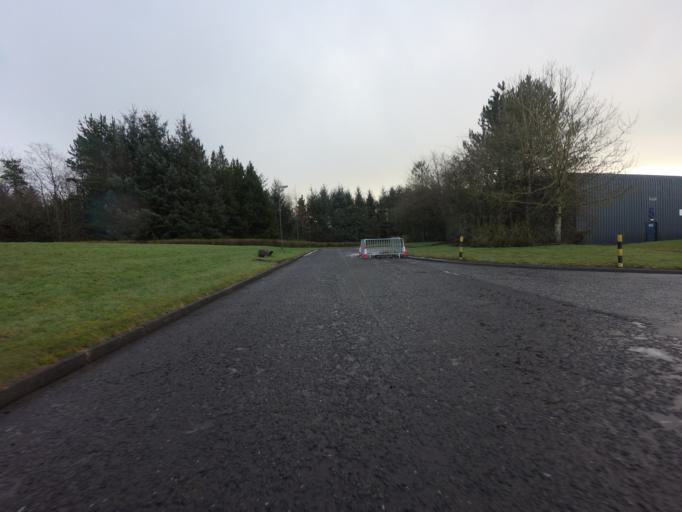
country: GB
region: Scotland
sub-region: West Lothian
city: West Calder
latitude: 55.8999
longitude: -3.5817
